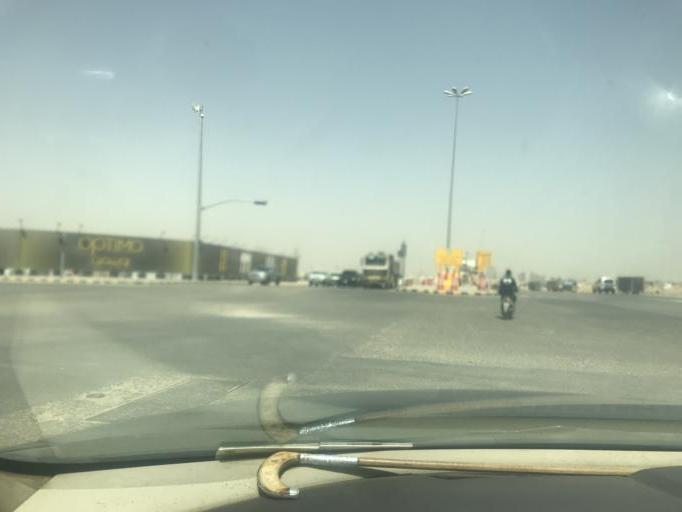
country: SA
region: Ar Riyad
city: Riyadh
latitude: 24.7952
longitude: 46.5862
